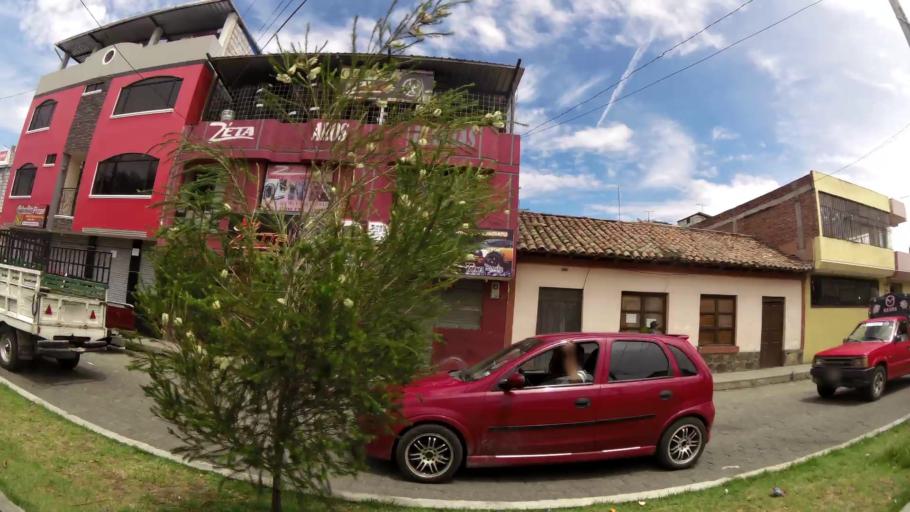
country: EC
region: Cotopaxi
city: San Miguel de Salcedo
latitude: -1.0455
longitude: -78.5897
